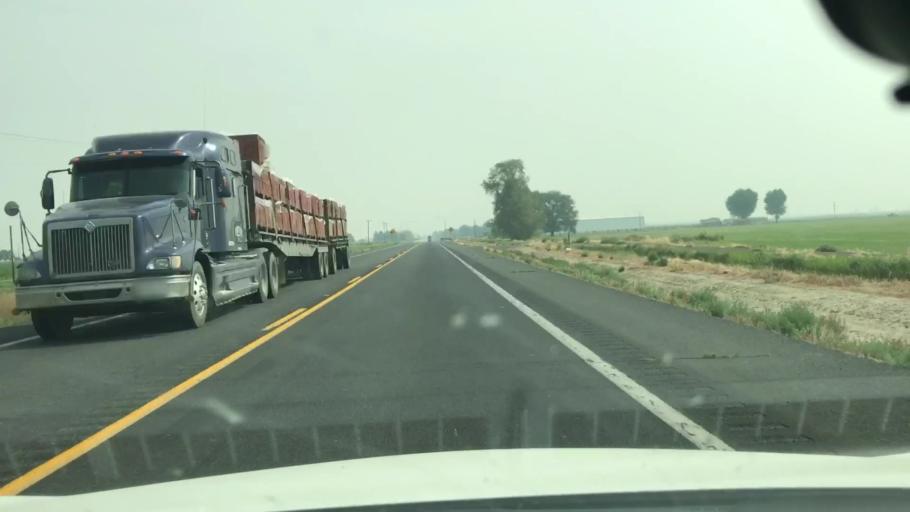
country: US
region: Washington
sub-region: Grant County
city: Quincy
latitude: 47.2342
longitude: -119.7747
